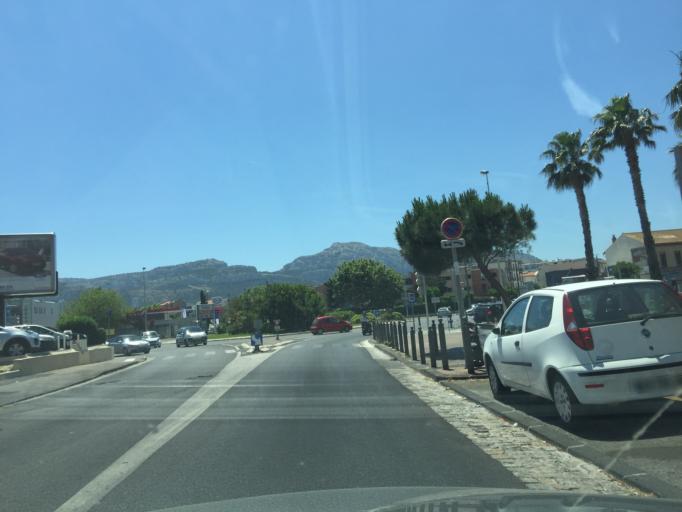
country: FR
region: Provence-Alpes-Cote d'Azur
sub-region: Departement des Bouches-du-Rhone
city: Marseille 08
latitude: 43.2550
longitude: 5.3821
